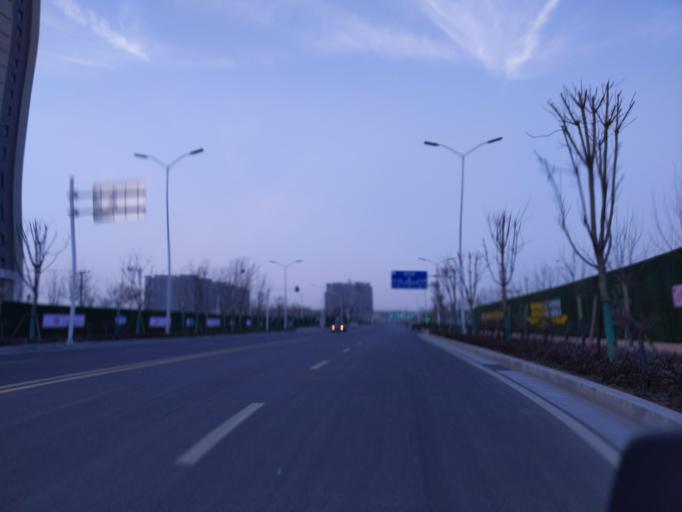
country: CN
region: Henan Sheng
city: Puyang
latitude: 35.8088
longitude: 115.0115
